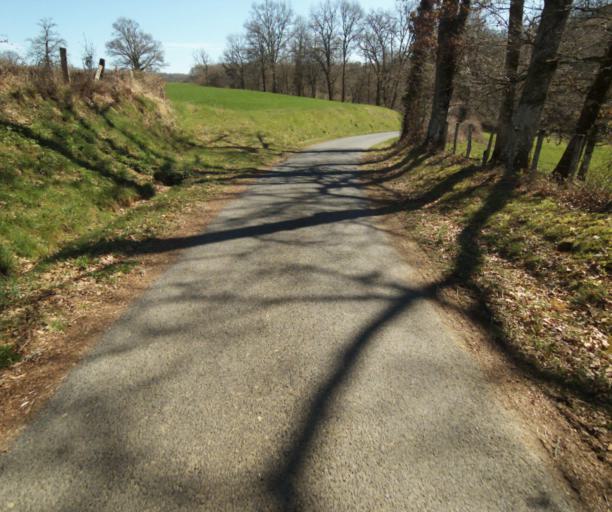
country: FR
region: Limousin
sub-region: Departement de la Correze
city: Chamboulive
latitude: 45.4546
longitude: 1.6887
